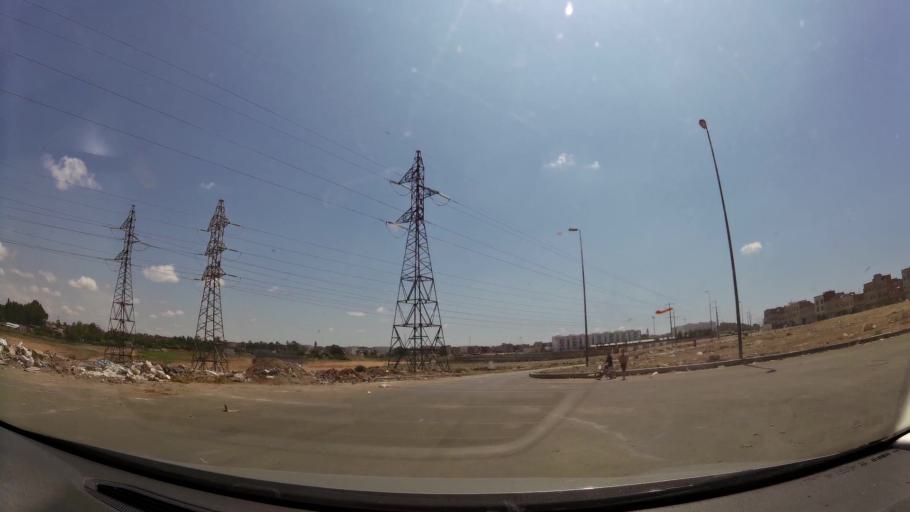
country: MA
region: Gharb-Chrarda-Beni Hssen
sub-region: Kenitra Province
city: Kenitra
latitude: 34.2381
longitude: -6.5377
